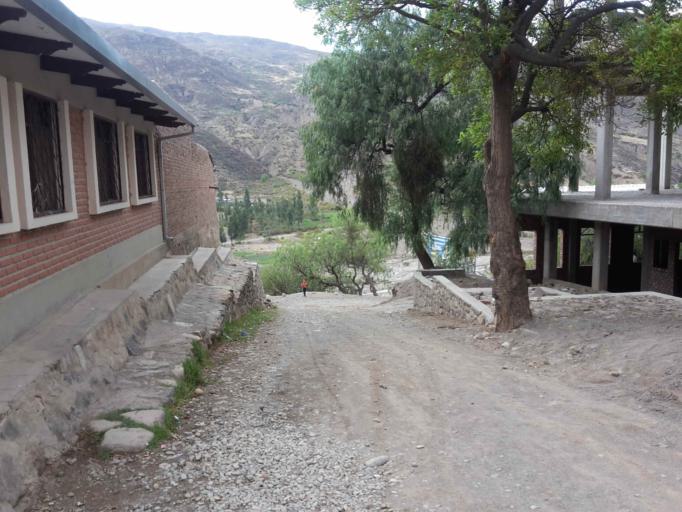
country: BO
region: Cochabamba
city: Colchani
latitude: -17.5167
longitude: -66.6186
